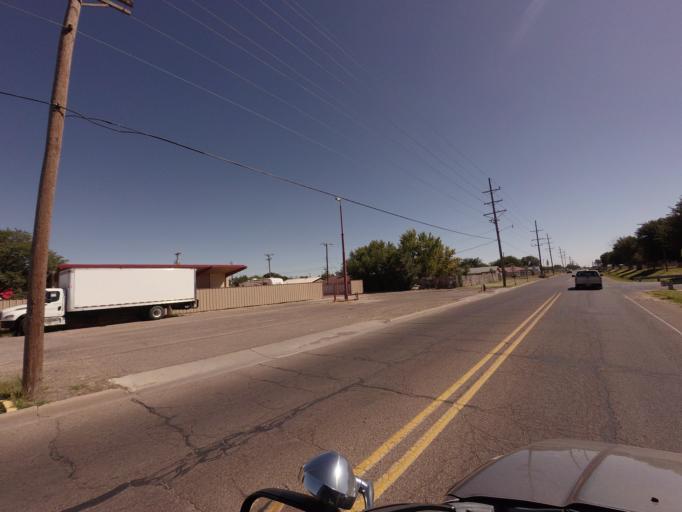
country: US
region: New Mexico
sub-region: Curry County
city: Clovis
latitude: 34.4102
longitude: -103.2318
